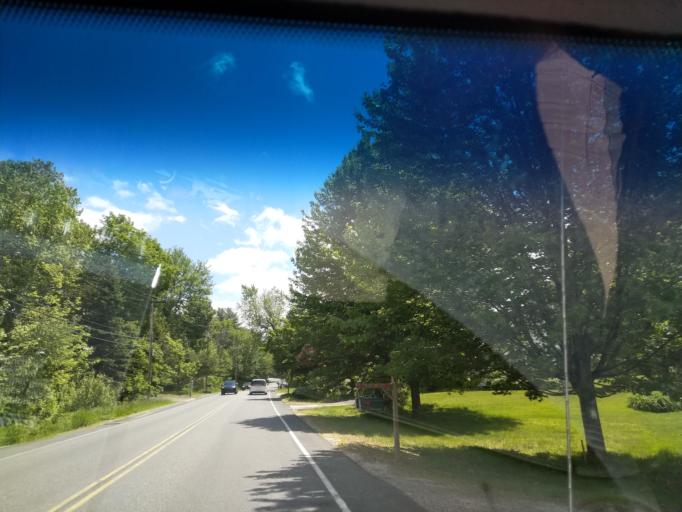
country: US
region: Maine
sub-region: Cumberland County
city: Falmouth
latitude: 43.7290
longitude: -70.2762
